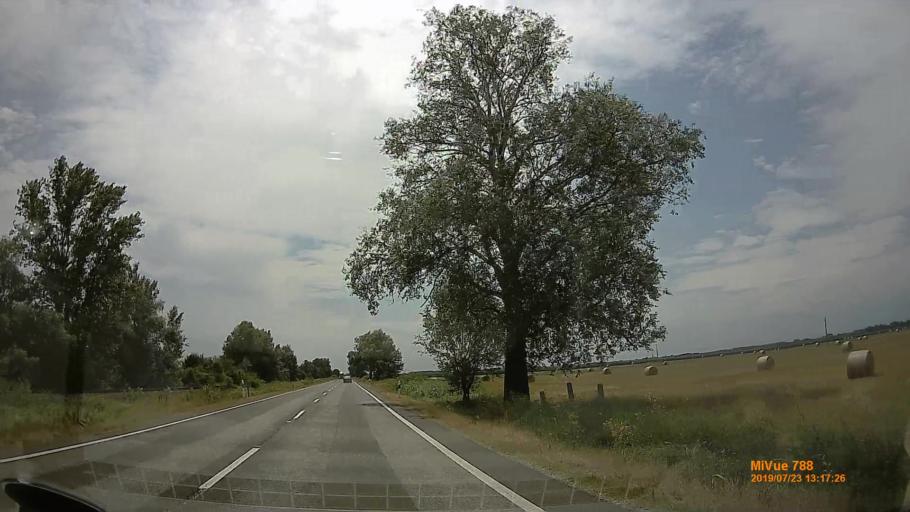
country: HU
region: Hajdu-Bihar
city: Polgar
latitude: 47.8990
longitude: 21.1571
